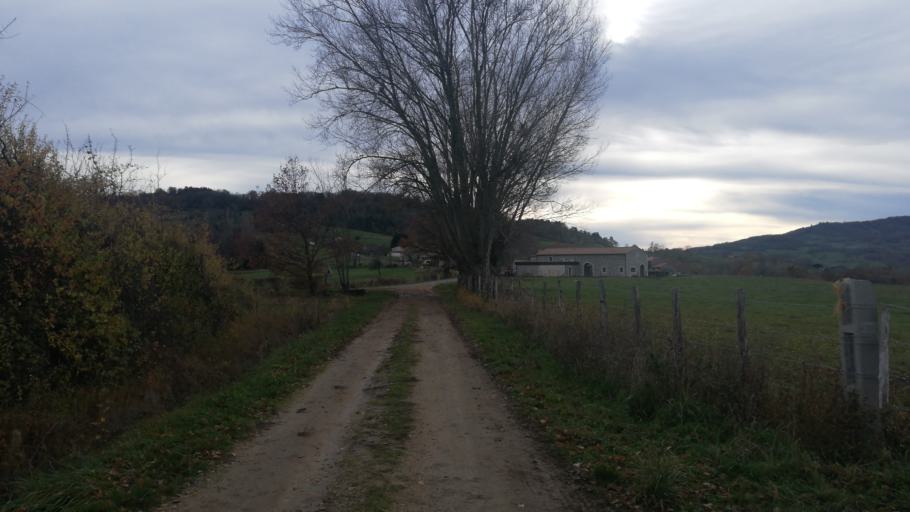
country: FR
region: Auvergne
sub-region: Departement du Puy-de-Dome
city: Billom
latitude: 45.6903
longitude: 3.3691
